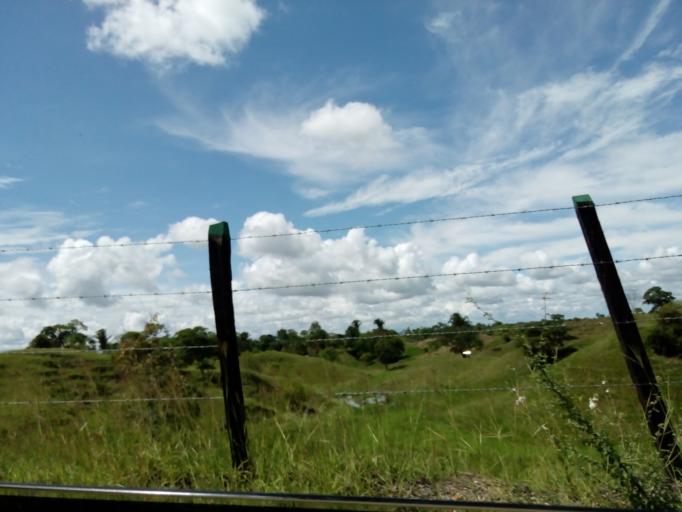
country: CO
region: Boyaca
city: Puerto Boyaca
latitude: 5.9607
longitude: -74.4571
